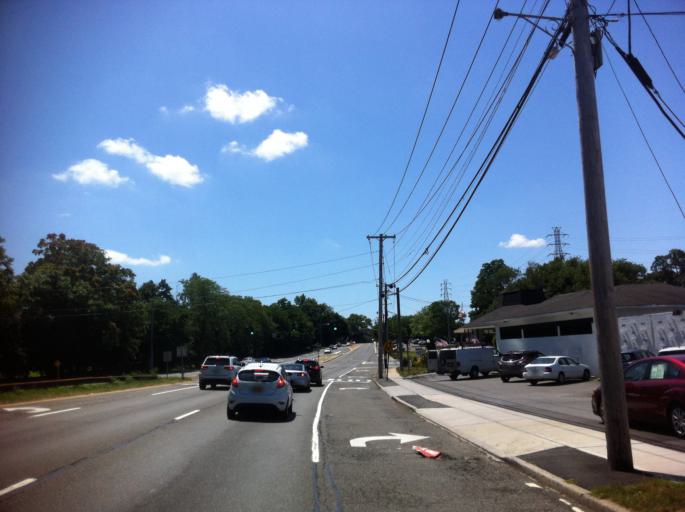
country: US
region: New York
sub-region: Nassau County
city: Greenvale
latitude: 40.8178
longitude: -73.6256
